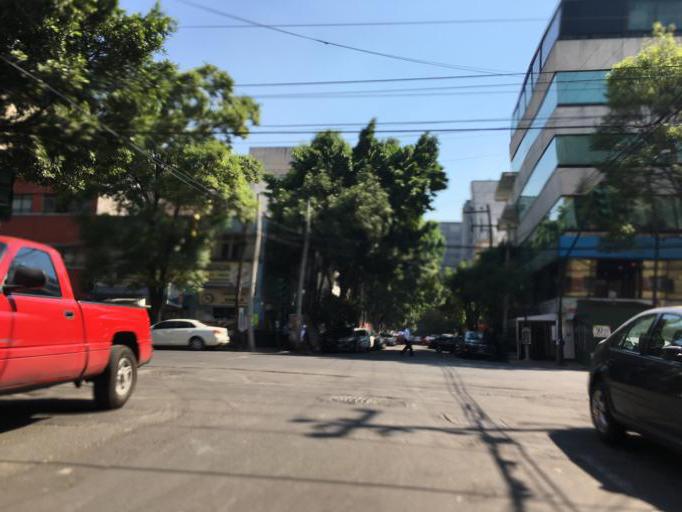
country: MX
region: Mexico City
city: Miguel Hidalgo
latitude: 19.4375
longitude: -99.1770
